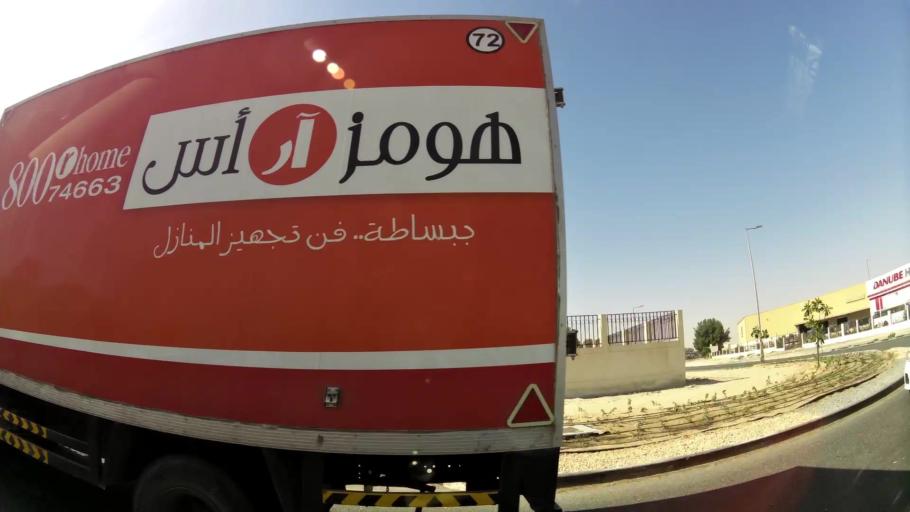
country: AE
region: Dubai
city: Dubai
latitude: 24.9389
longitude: 55.0672
